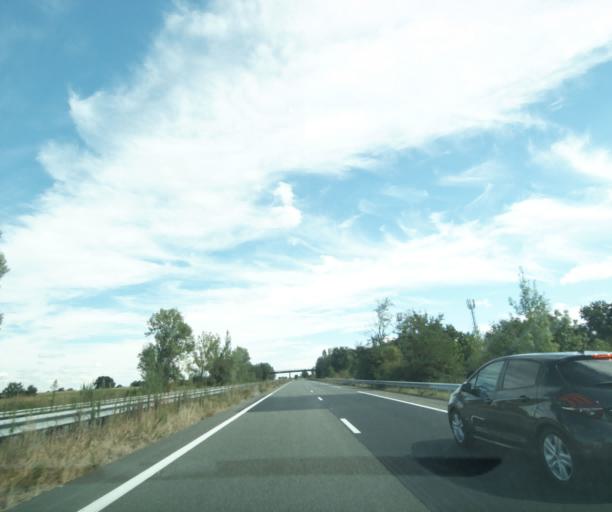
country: FR
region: Midi-Pyrenees
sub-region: Departement du Tarn-et-Garonne
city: Auvillar
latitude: 44.0564
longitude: 0.9509
